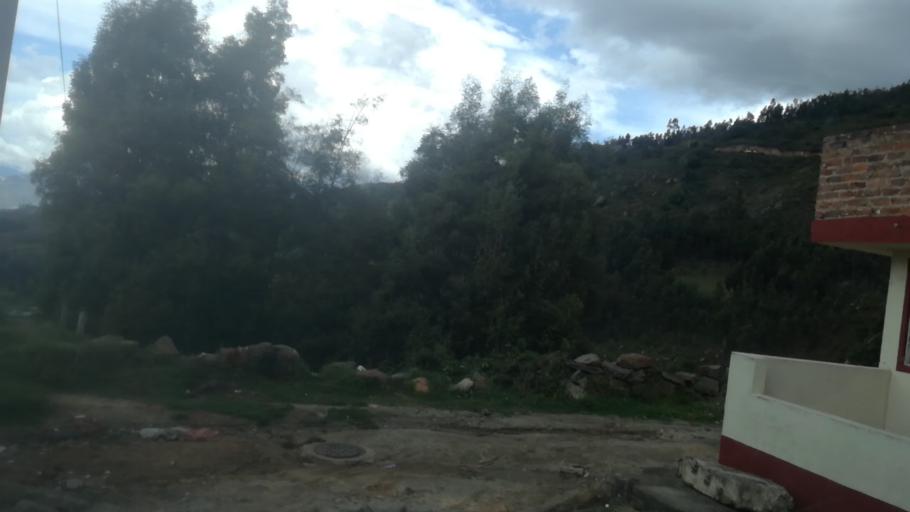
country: CO
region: Boyaca
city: Socha Viejo
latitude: 6.0009
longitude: -72.6891
